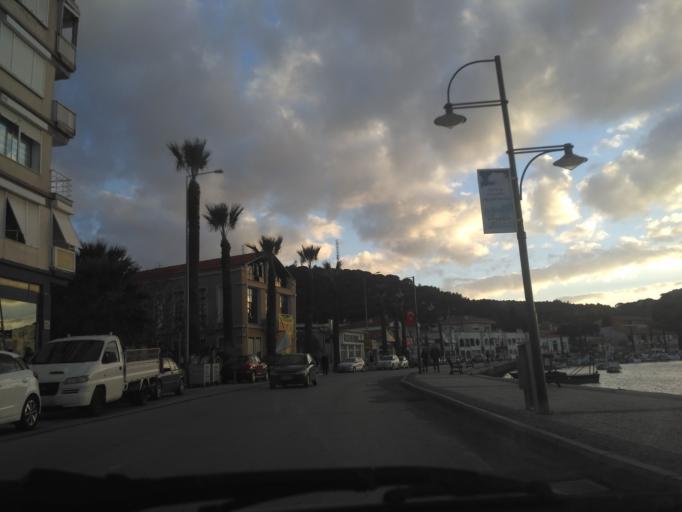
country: TR
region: Balikesir
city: Ayvalik
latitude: 39.3145
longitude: 26.6902
